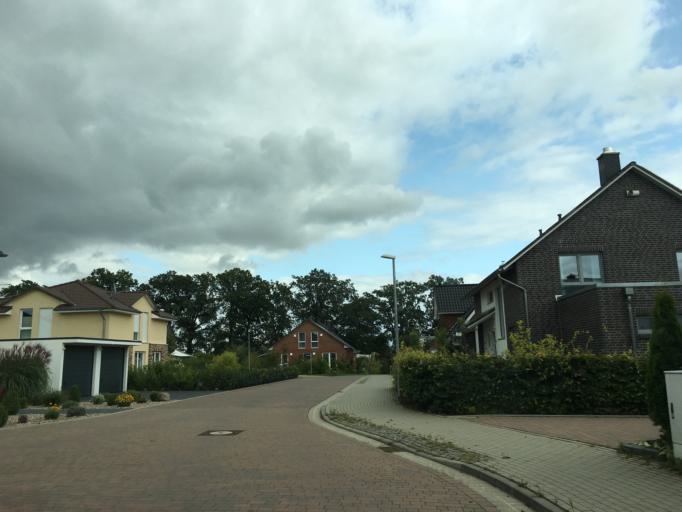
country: DE
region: Lower Saxony
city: Embsen
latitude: 53.2085
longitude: 10.3750
